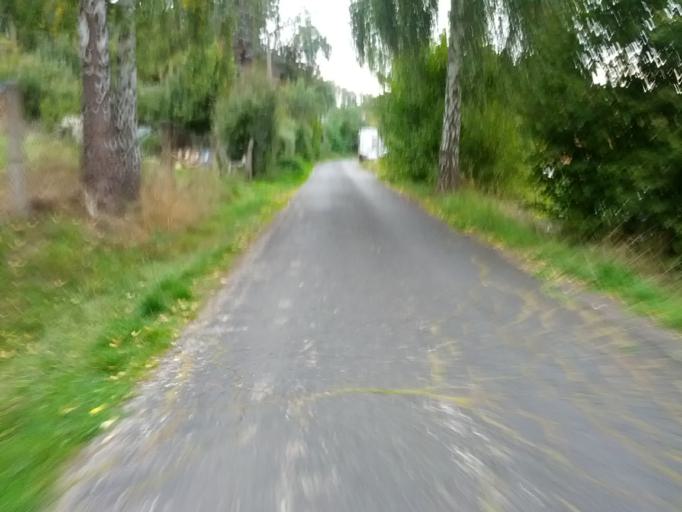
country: DE
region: Thuringia
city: Thal
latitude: 50.9399
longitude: 10.3895
